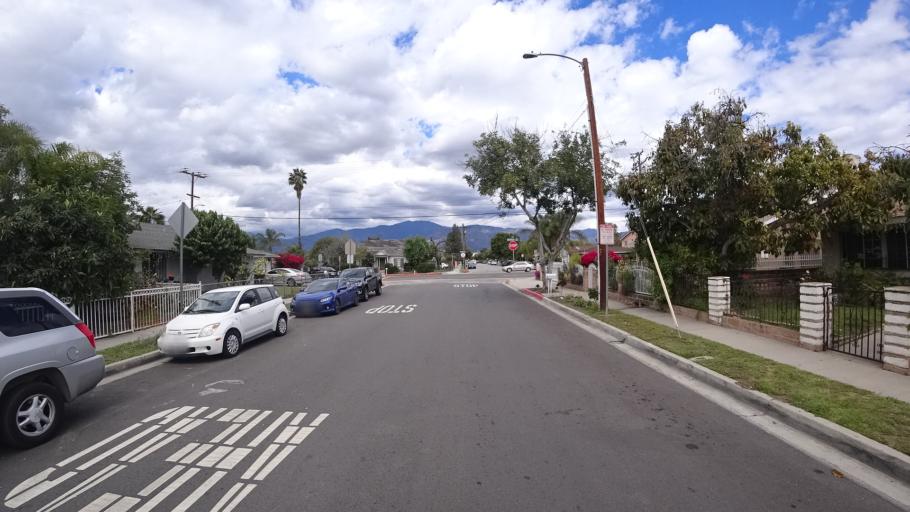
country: US
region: California
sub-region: Los Angeles County
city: Baldwin Park
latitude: 34.0991
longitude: -117.9552
